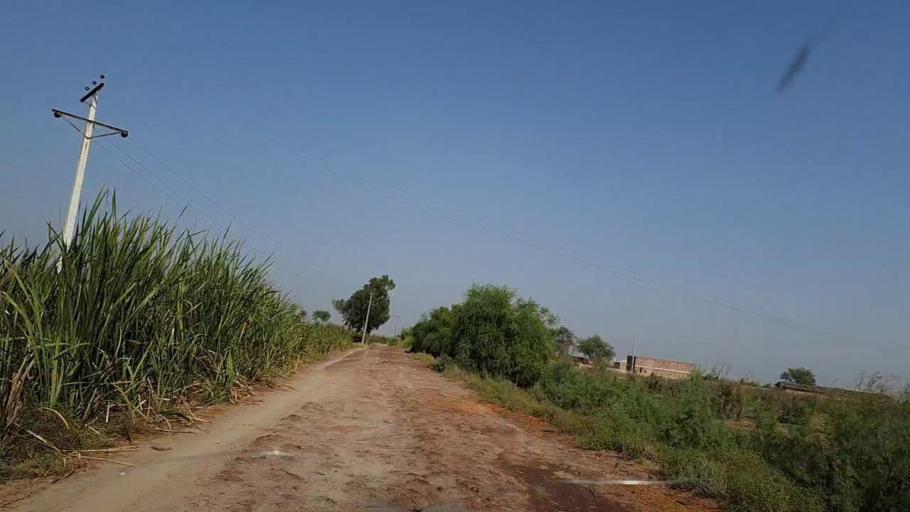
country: PK
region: Sindh
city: Khanpur
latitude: 27.6756
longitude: 69.3737
